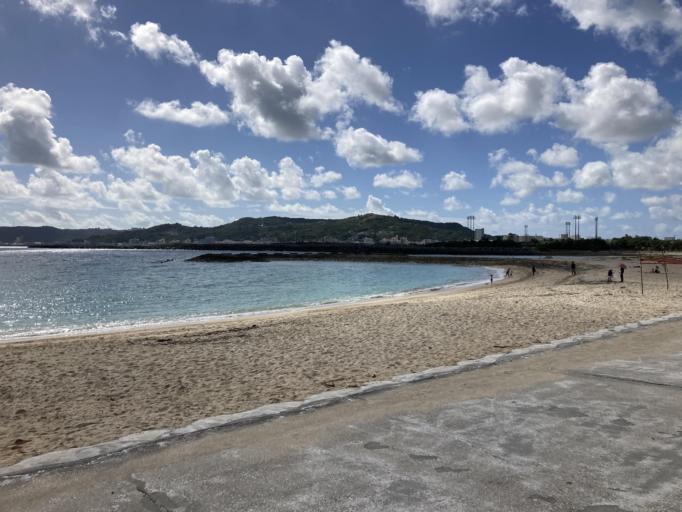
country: JP
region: Okinawa
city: Ginowan
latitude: 26.2124
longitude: 127.7717
